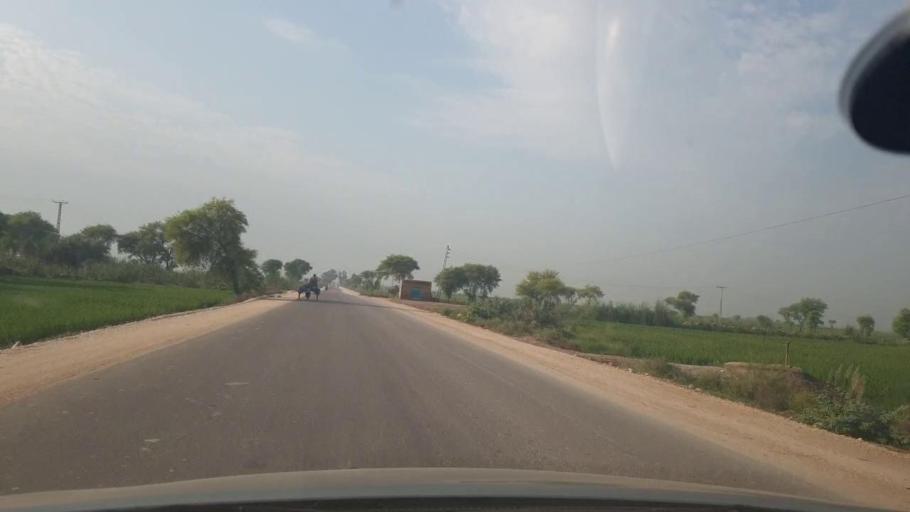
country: PK
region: Sindh
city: Jacobabad
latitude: 28.1917
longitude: 68.3675
